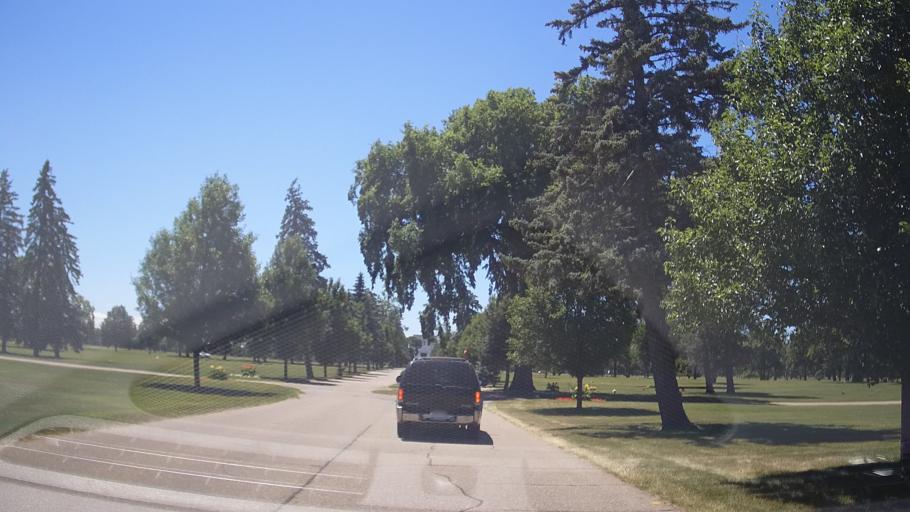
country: US
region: Michigan
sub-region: Oakland County
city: Troy
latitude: 42.5894
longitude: -83.1637
